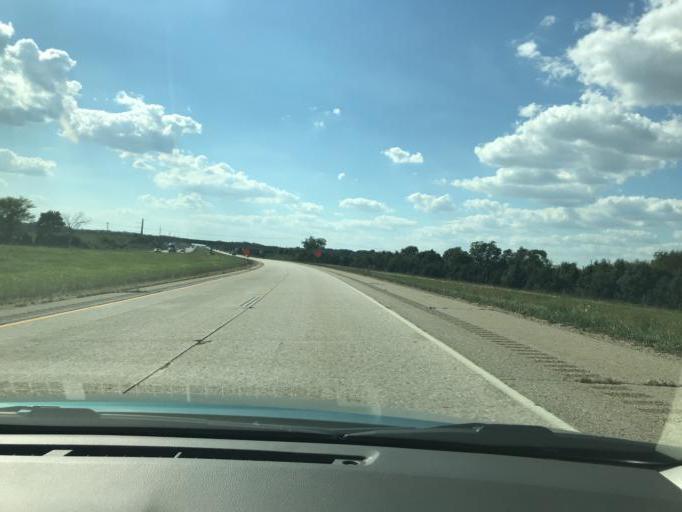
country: US
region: Wisconsin
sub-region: Walworth County
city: Delavan
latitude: 42.6213
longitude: -88.6738
